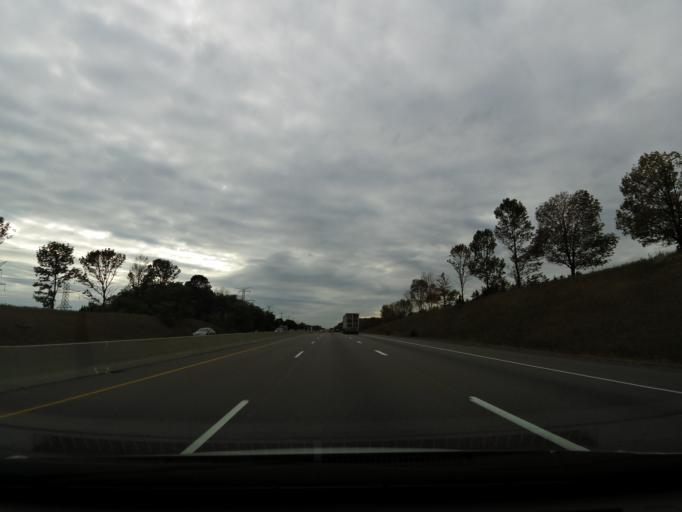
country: CA
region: Ontario
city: Cobourg
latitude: 43.9372
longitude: -78.4620
